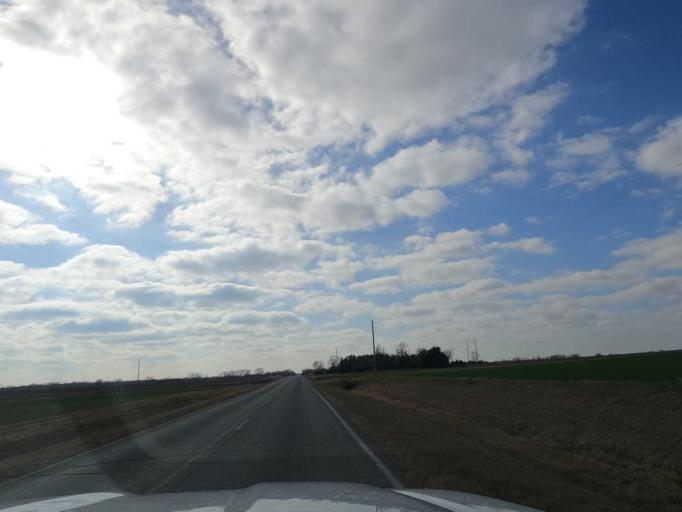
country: US
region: Kansas
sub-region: McPherson County
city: Inman
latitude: 38.2321
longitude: -97.8654
